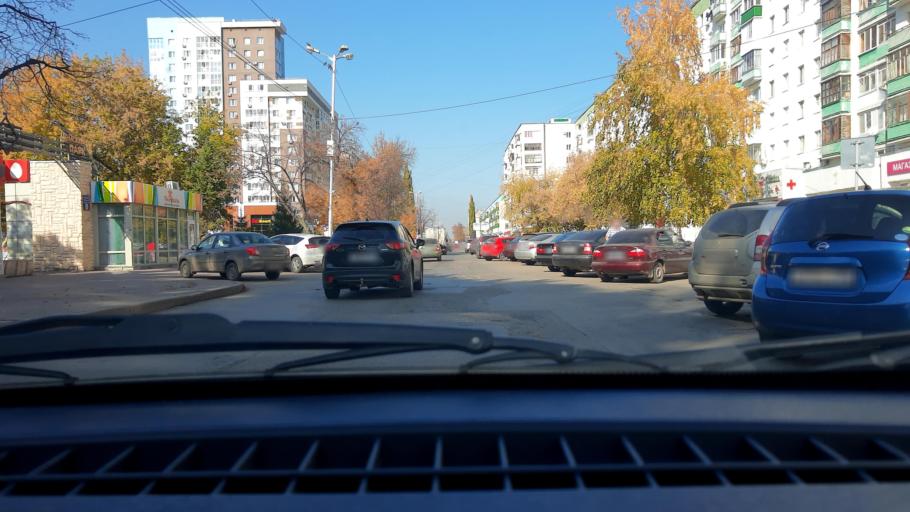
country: RU
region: Bashkortostan
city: Avdon
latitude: 54.7031
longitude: 55.8301
